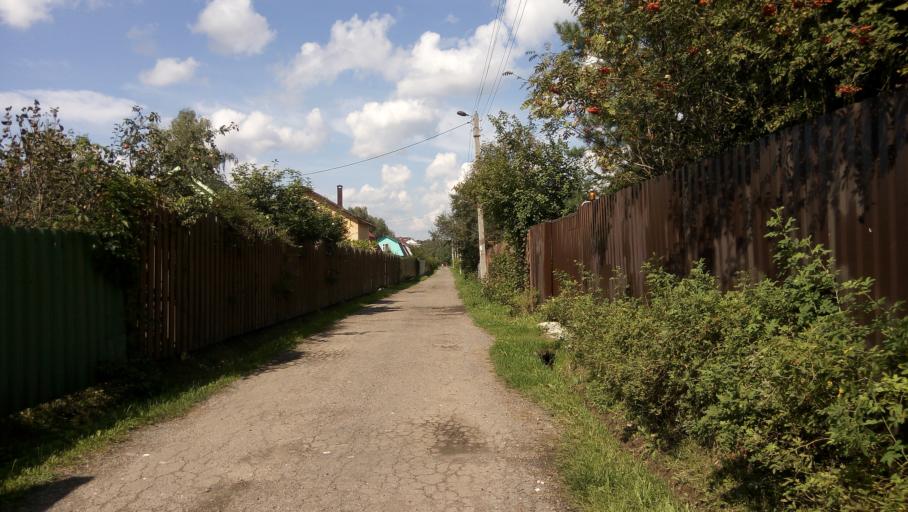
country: RU
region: Moskovskaya
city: Proletarskiy
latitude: 55.0551
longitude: 37.4012
